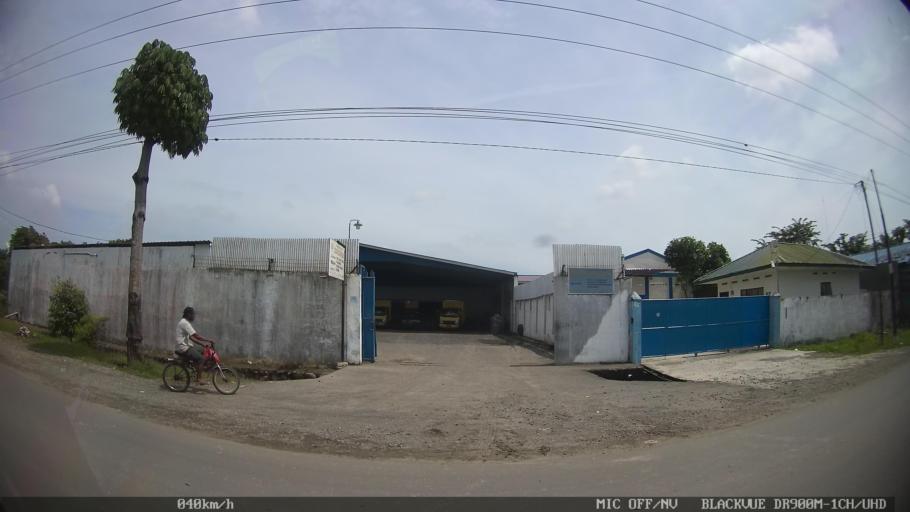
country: ID
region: North Sumatra
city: Medan
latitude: 3.6504
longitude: 98.7123
